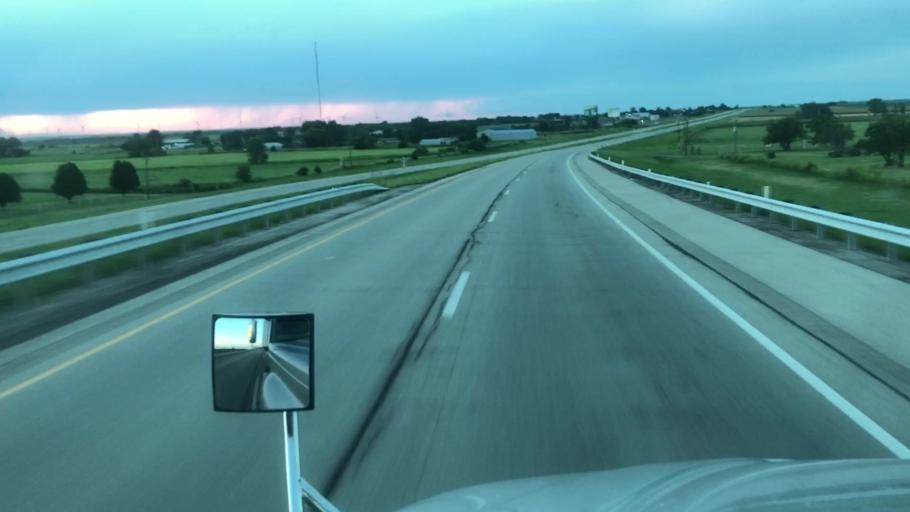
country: US
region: Oklahoma
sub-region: Kay County
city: Ponca City
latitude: 36.7768
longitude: -97.0665
